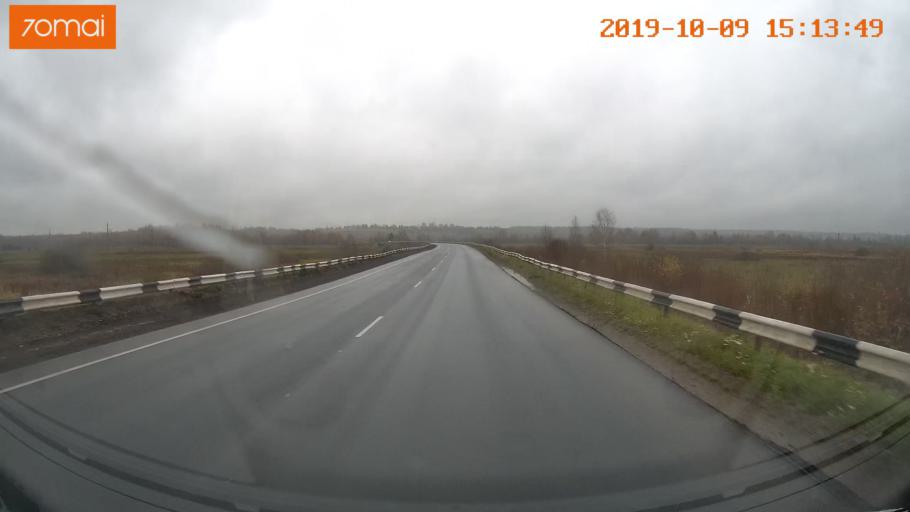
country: RU
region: Kostroma
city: Susanino
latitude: 58.1433
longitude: 41.6125
